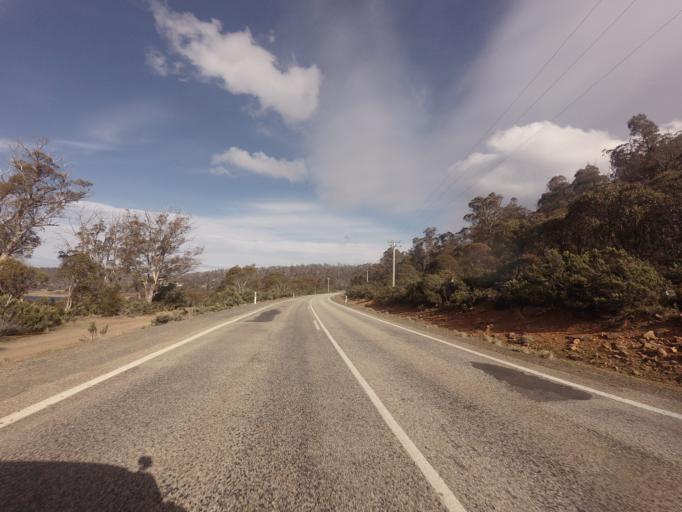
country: AU
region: Tasmania
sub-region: Meander Valley
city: Deloraine
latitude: -41.9837
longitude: 146.6794
